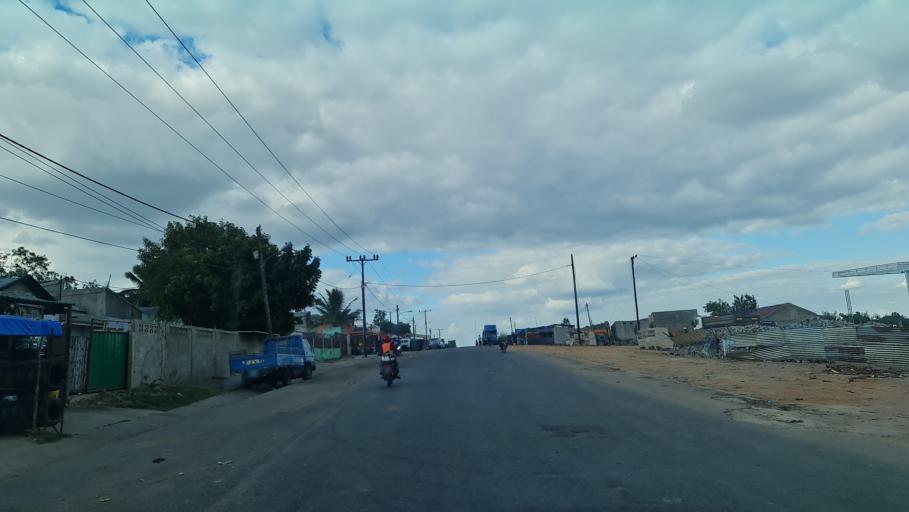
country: MZ
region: Manica
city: Chimoio
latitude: -19.2101
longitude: 33.9269
